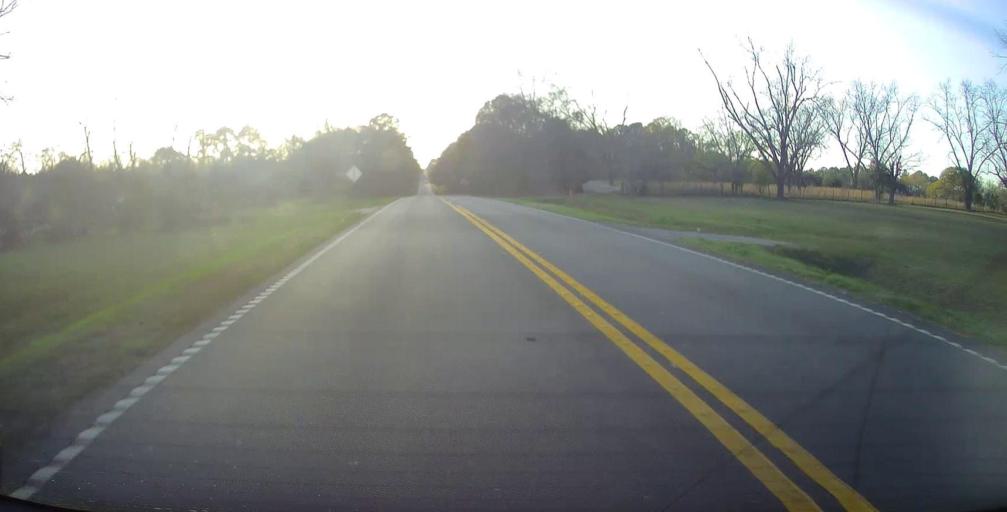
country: US
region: Georgia
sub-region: Evans County
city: Claxton
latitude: 32.1524
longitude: -81.8241
